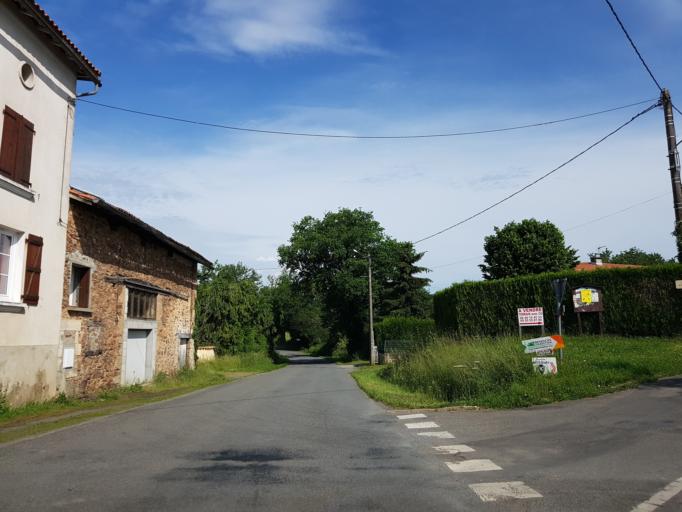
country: FR
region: Poitou-Charentes
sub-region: Departement de la Charente
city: Chabanais
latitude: 45.8799
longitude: 0.7132
